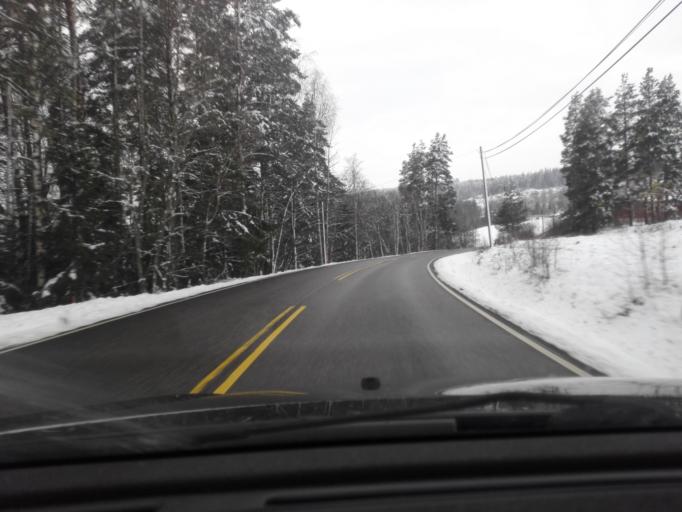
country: FI
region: Uusimaa
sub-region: Helsinki
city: Vihti
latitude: 60.4191
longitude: 24.3710
